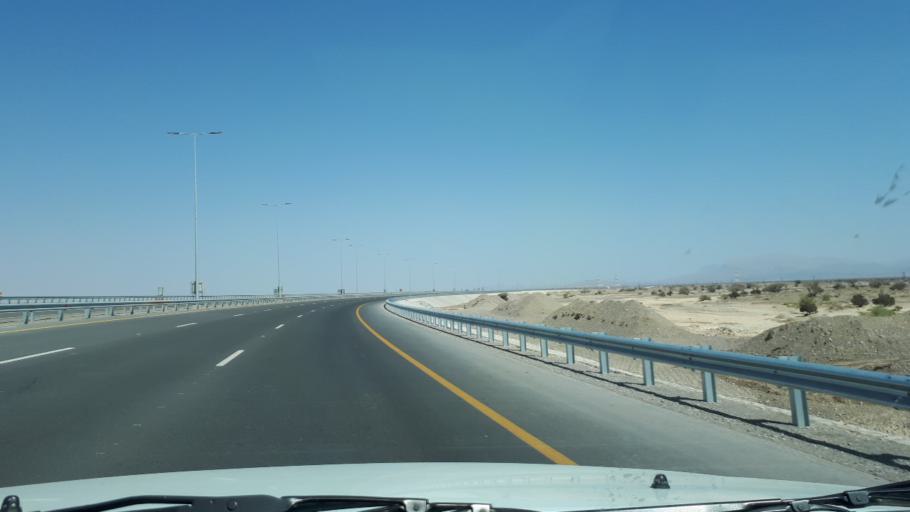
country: OM
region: Ash Sharqiyah
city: Badiyah
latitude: 22.2882
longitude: 59.1518
